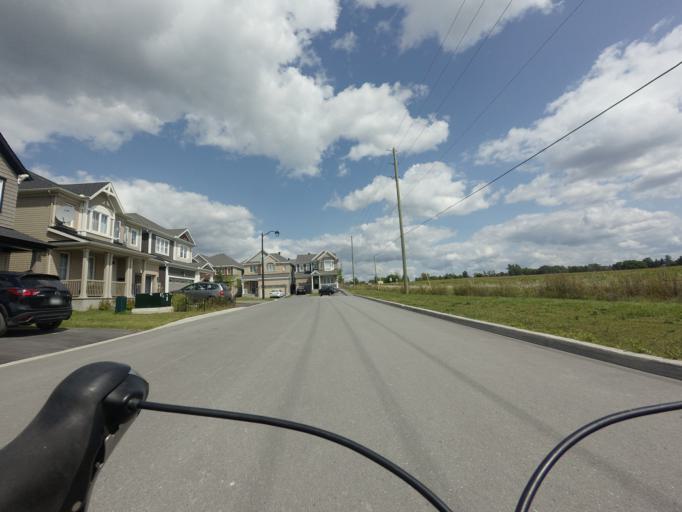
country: CA
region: Ontario
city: Bells Corners
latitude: 45.2751
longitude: -75.8418
